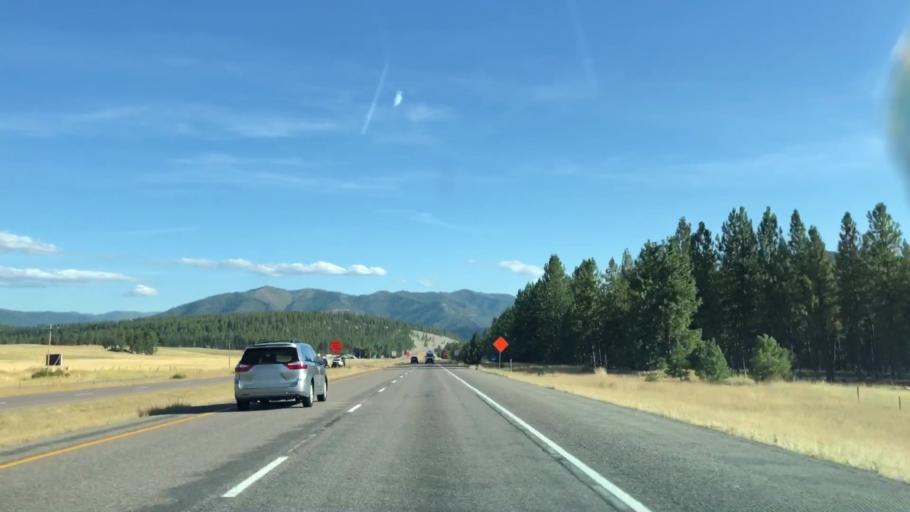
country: US
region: Montana
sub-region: Mineral County
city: Superior
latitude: 47.0381
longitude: -114.7464
